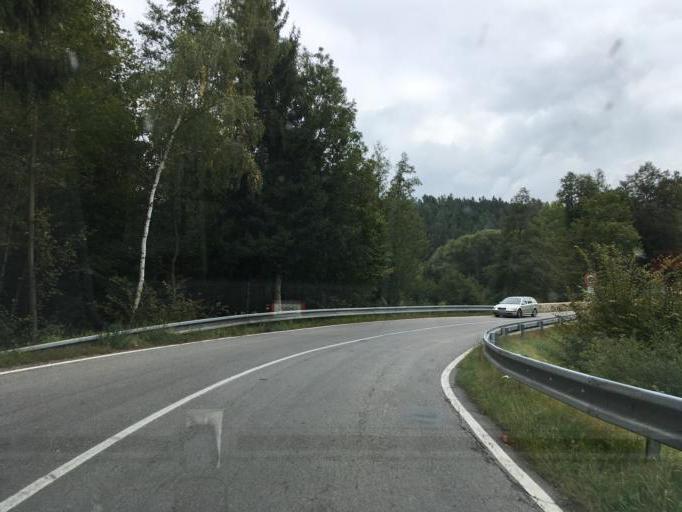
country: CZ
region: Vysocina
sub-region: Okres Pelhrimov
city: Zeliv
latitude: 49.5301
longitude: 15.1705
